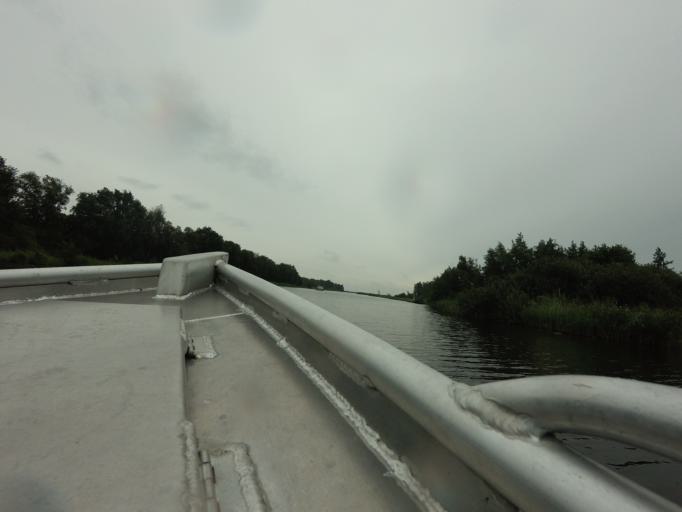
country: NL
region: Overijssel
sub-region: Gemeente Steenwijkerland
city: Sint Jansklooster
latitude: 52.7116
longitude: 6.0195
